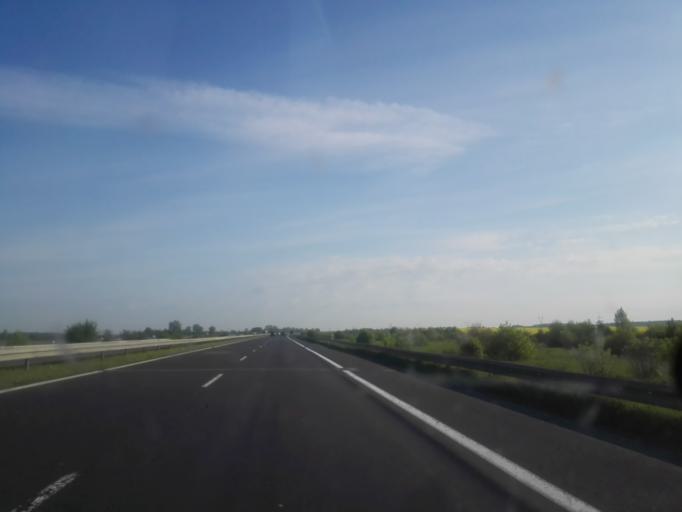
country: PL
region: Lodz Voivodeship
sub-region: Powiat radomszczanski
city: Kamiensk
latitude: 51.2681
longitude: 19.5309
